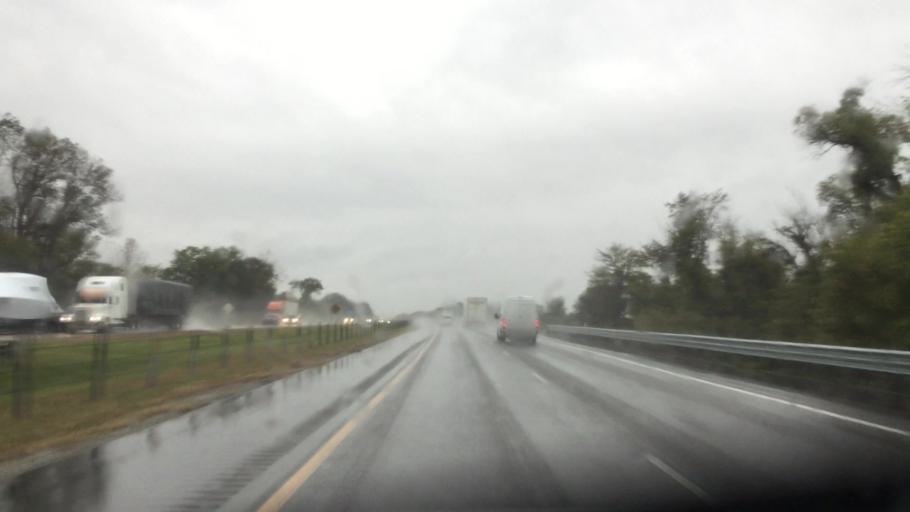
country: US
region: Michigan
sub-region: Van Buren County
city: Hartford
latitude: 42.1938
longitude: -86.1475
